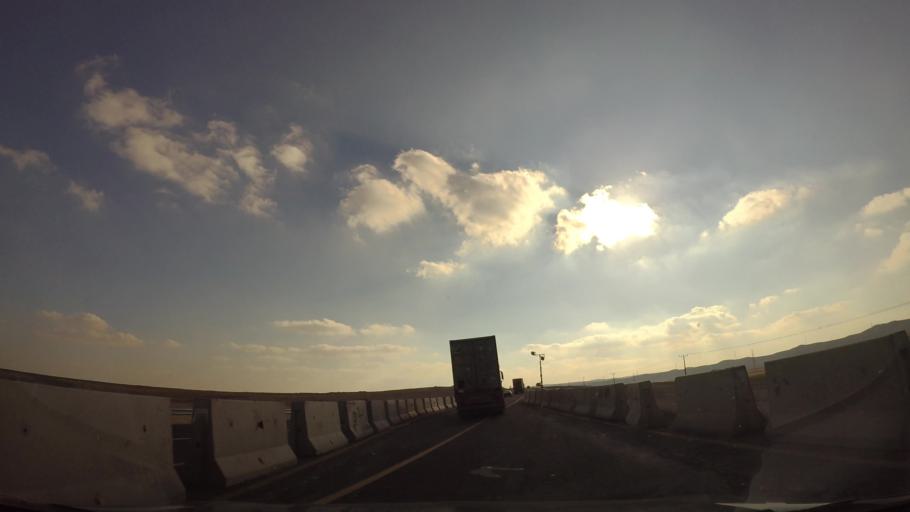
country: JO
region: Karak
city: Karak City
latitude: 31.1292
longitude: 36.0230
